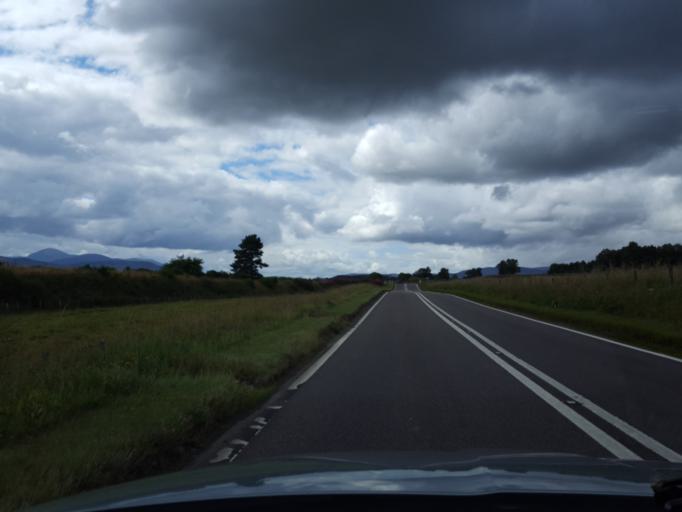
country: GB
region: Scotland
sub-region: Highland
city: Grantown on Spey
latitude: 57.2672
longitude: -3.7266
